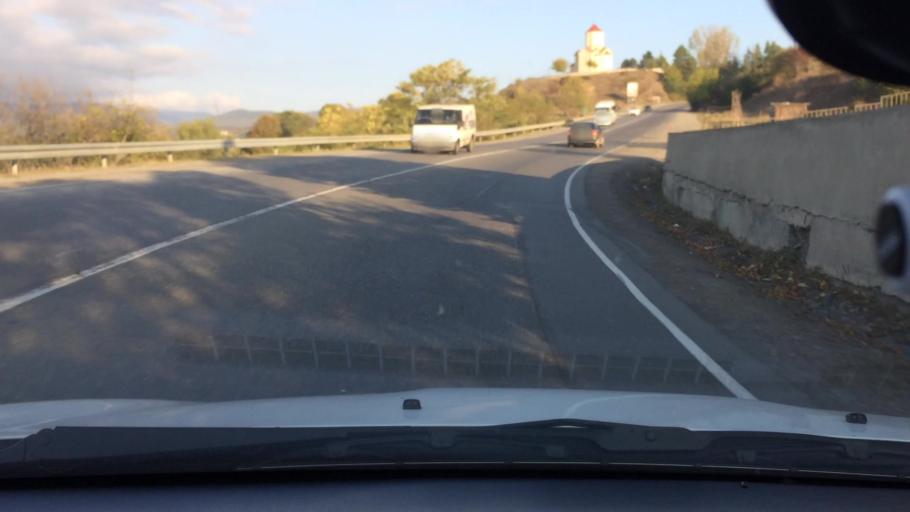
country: GE
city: Surami
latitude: 42.0180
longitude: 43.5673
